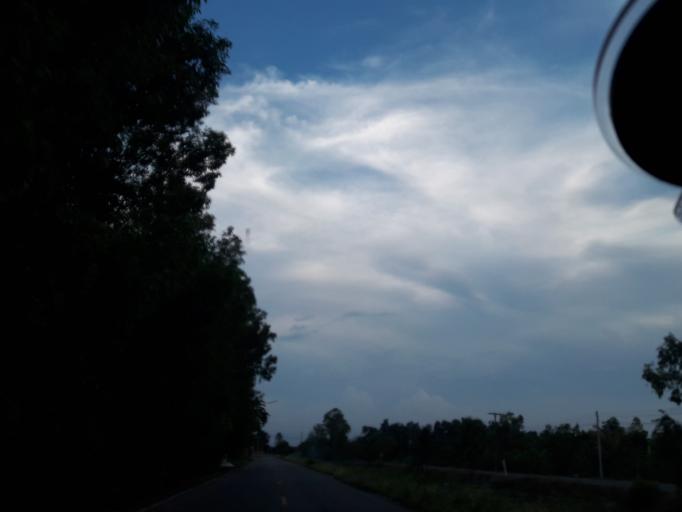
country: TH
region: Pathum Thani
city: Nong Suea
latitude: 14.2141
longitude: 100.8689
